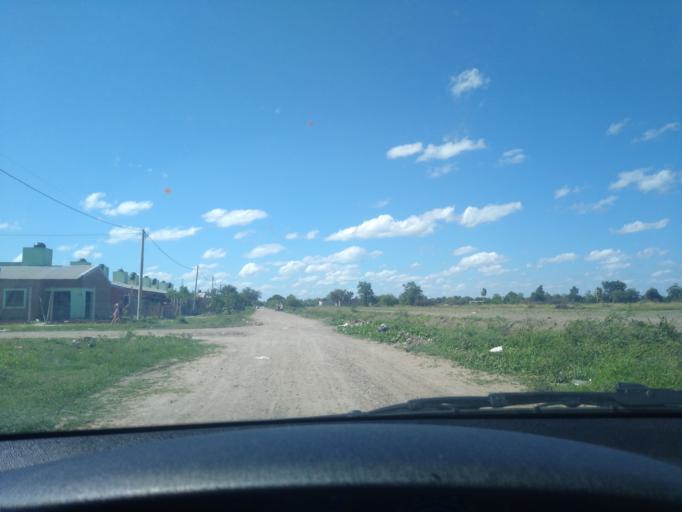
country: AR
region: Chaco
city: Resistencia
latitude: -27.4855
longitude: -59.0107
